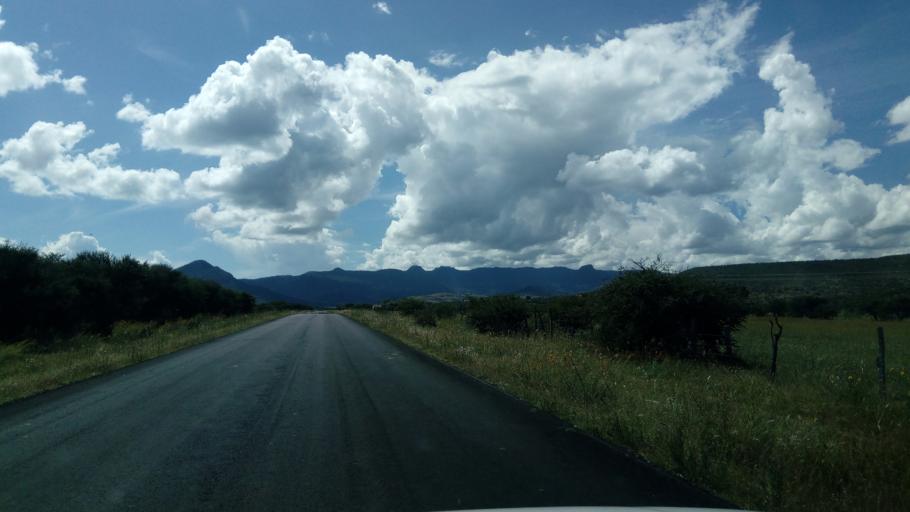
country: MX
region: Durango
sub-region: Durango
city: Jose Refugio Salcido
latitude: 23.8074
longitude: -104.4840
